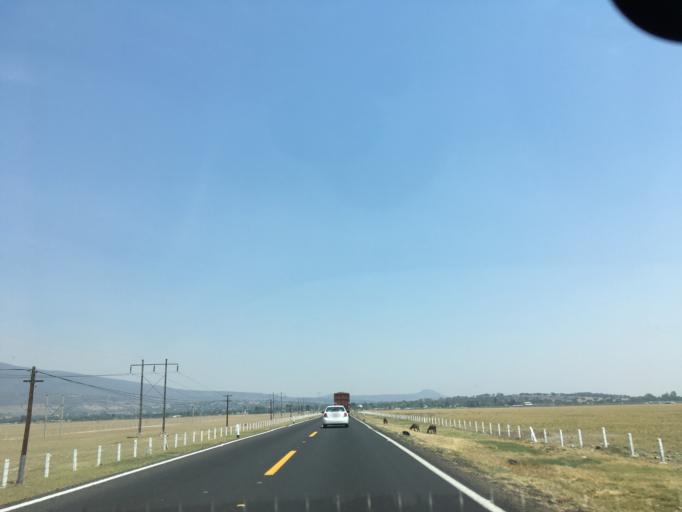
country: MX
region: Michoacan
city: Cuitzeo del Porvenir
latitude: 19.9806
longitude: -101.1442
